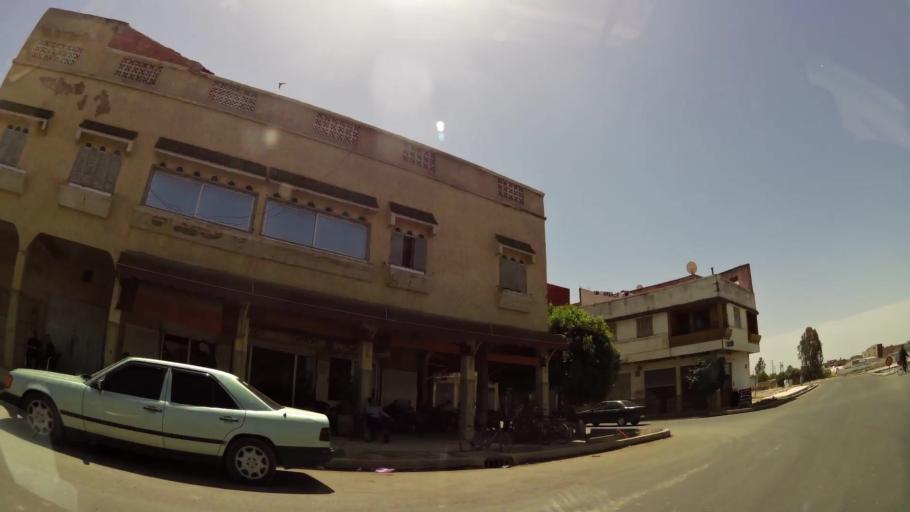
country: MA
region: Rabat-Sale-Zemmour-Zaer
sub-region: Khemisset
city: Khemisset
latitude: 33.8117
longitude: -6.0761
